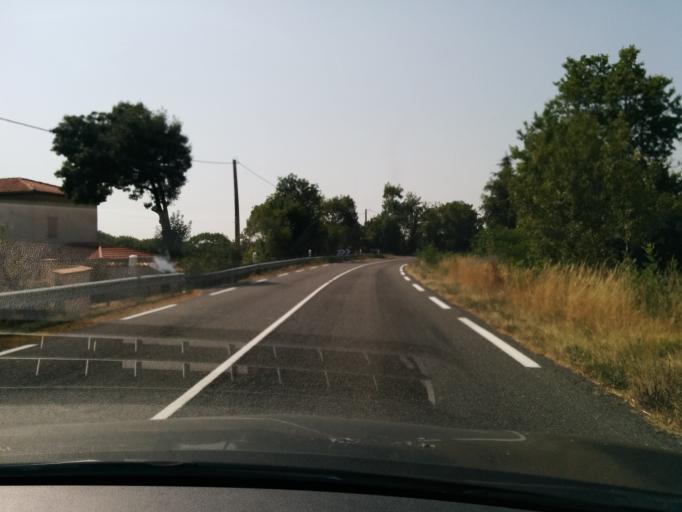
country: FR
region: Midi-Pyrenees
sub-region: Departement du Tarn
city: Castelnau-de-Levis
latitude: 43.9713
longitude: 2.0957
